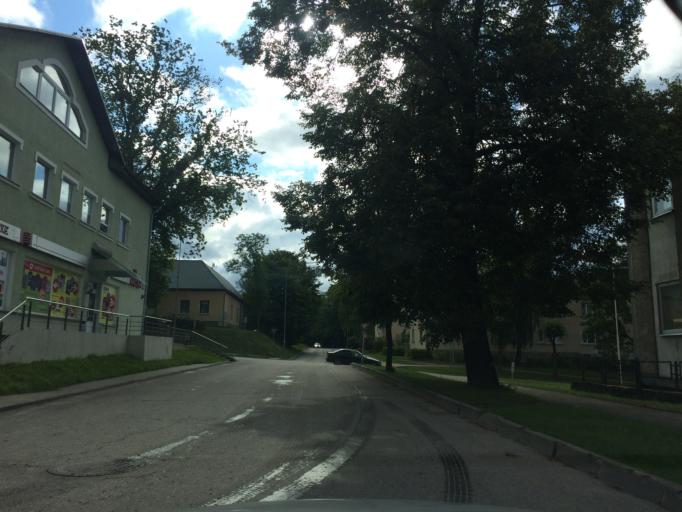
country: LV
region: Rezekne
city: Rezekne
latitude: 56.5044
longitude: 27.3319
